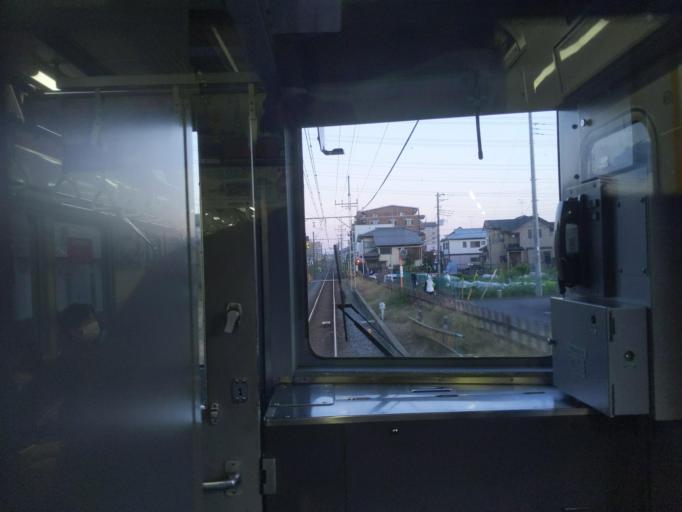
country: JP
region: Chiba
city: Noda
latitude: 35.9239
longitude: 139.8987
